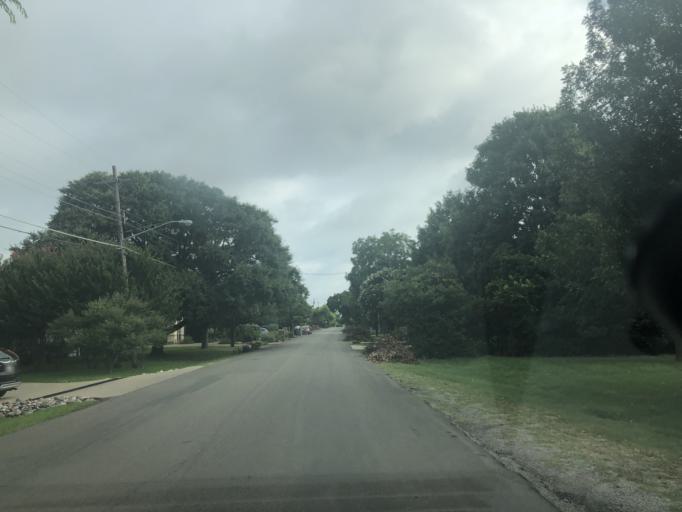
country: US
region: Texas
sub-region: Dallas County
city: University Park
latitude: 32.8518
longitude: -96.8398
